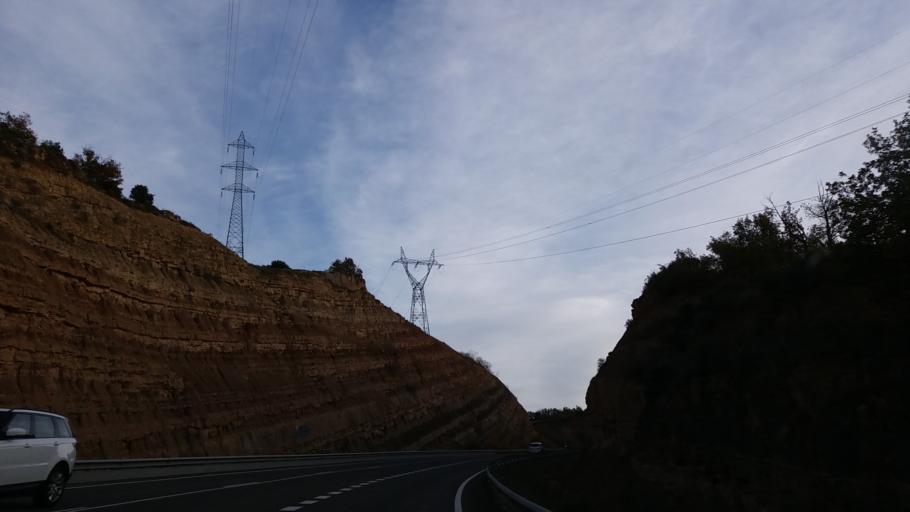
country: ES
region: Catalonia
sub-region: Provincia de Lleida
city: Ponts
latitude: 41.9213
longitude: 1.2058
